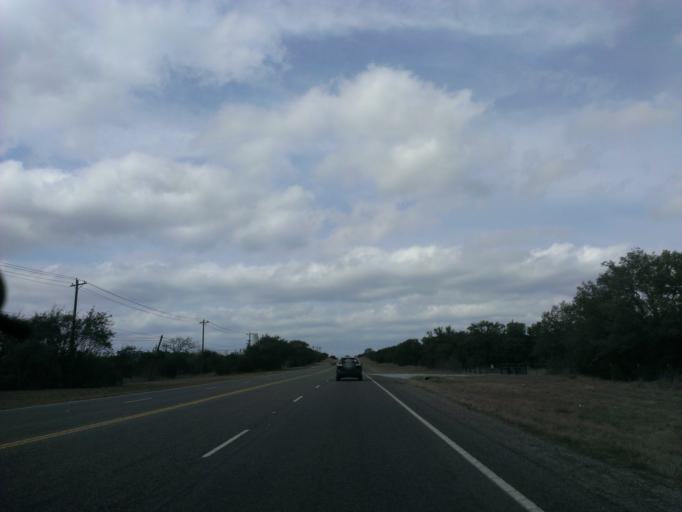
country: US
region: Texas
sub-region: Burnet County
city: Marble Falls
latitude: 30.4847
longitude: -98.2052
